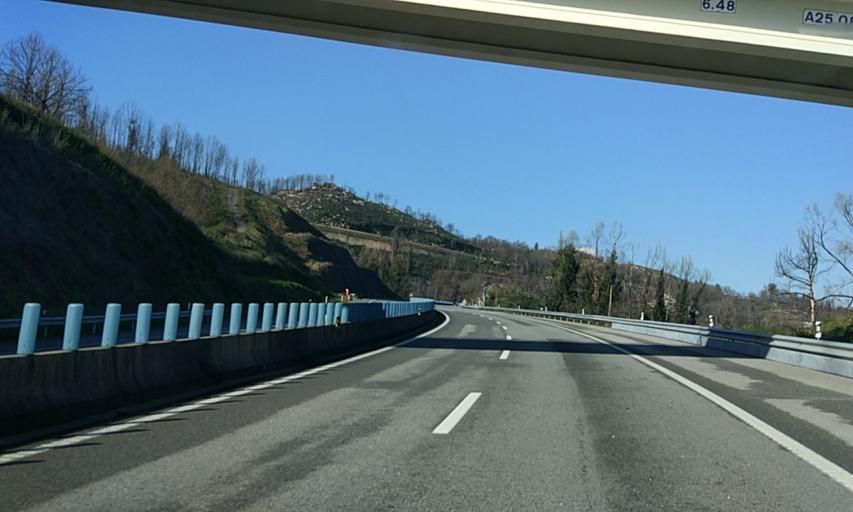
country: PT
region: Viseu
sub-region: Vouzela
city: Vouzela
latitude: 40.7002
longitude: -8.1037
